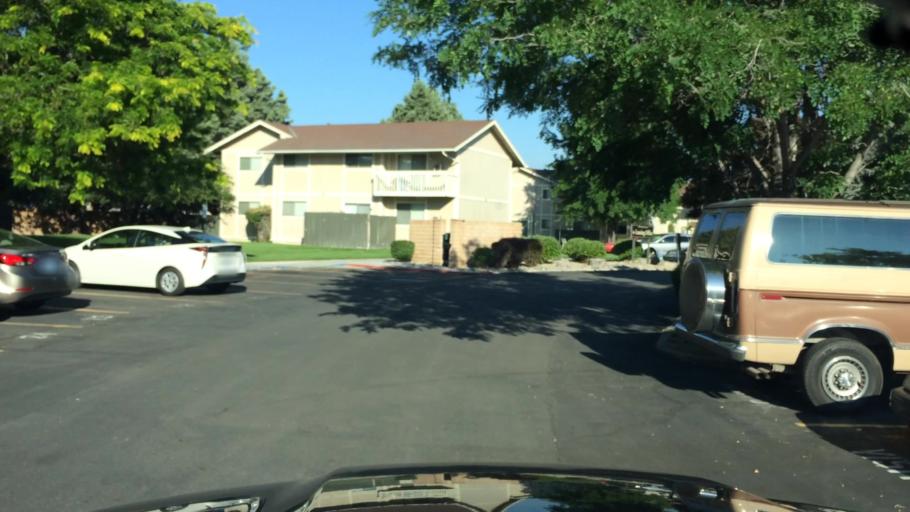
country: US
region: Nevada
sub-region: Washoe County
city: Sparks
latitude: 39.5451
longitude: -119.7555
